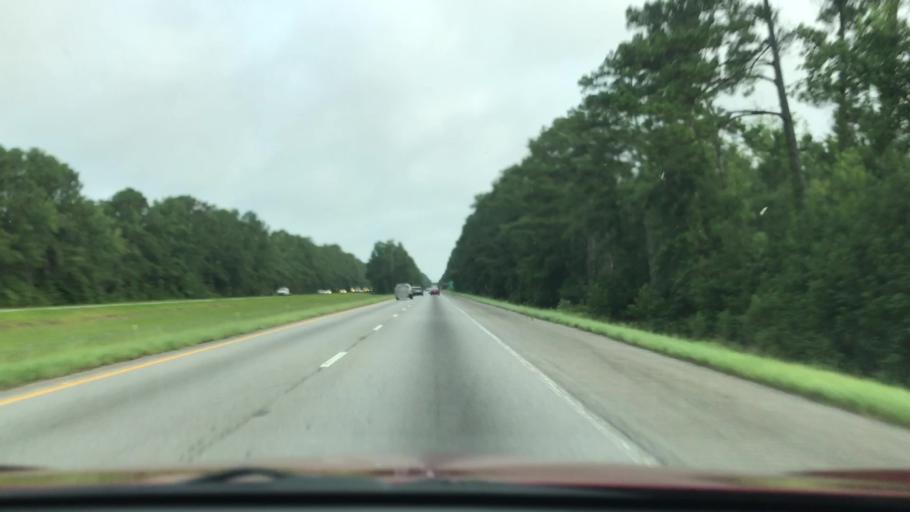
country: US
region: South Carolina
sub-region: Orangeburg County
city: Holly Hill
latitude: 33.2995
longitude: -80.5294
